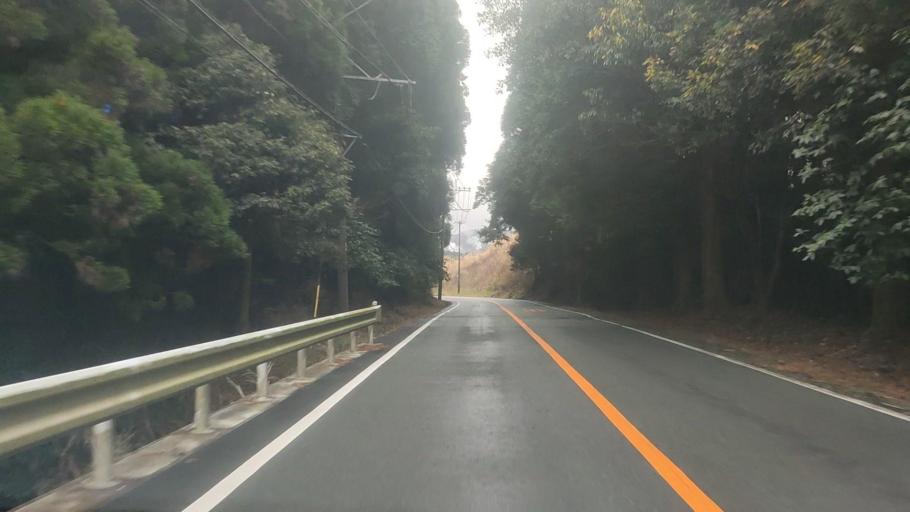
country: JP
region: Kumamoto
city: Aso
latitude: 32.8917
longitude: 131.0204
